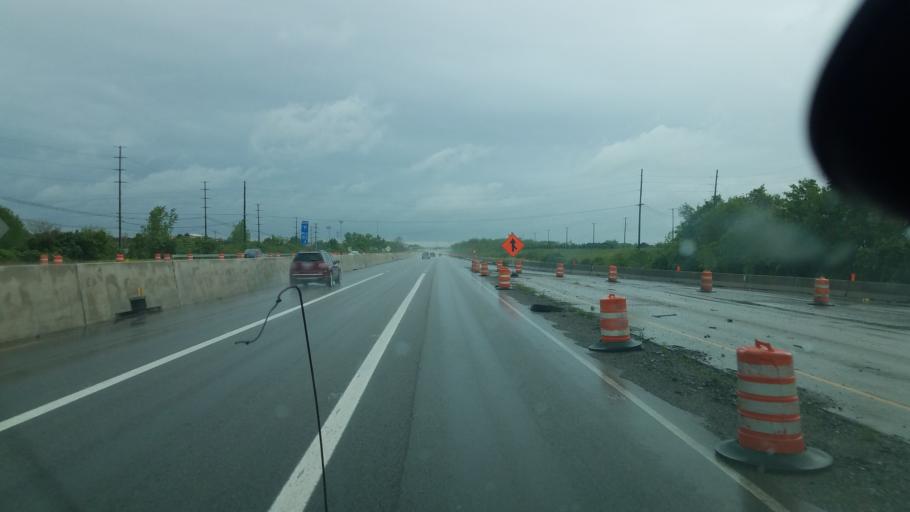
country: US
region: Ohio
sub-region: Franklin County
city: Columbus
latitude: 39.9127
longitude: -83.0209
